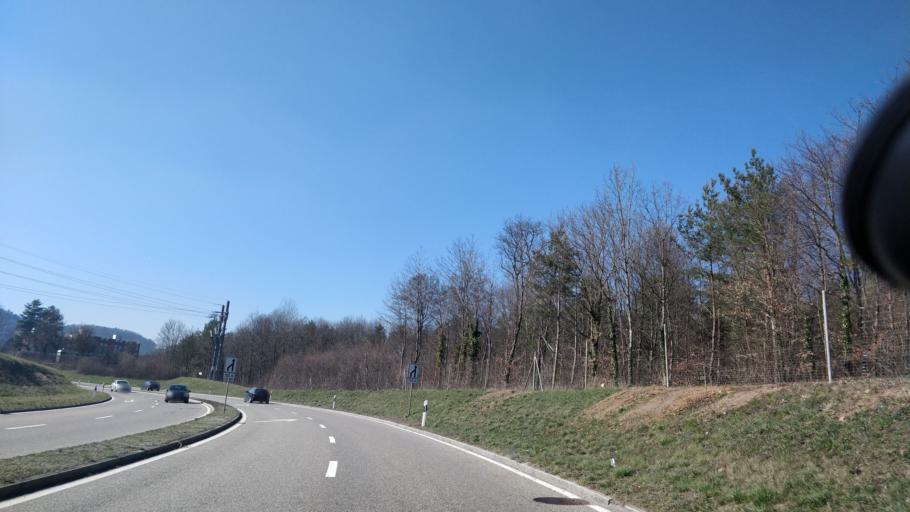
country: CH
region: Zurich
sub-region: Bezirk Buelach
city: Embrach / Kellersacker
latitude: 47.5230
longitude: 8.5934
